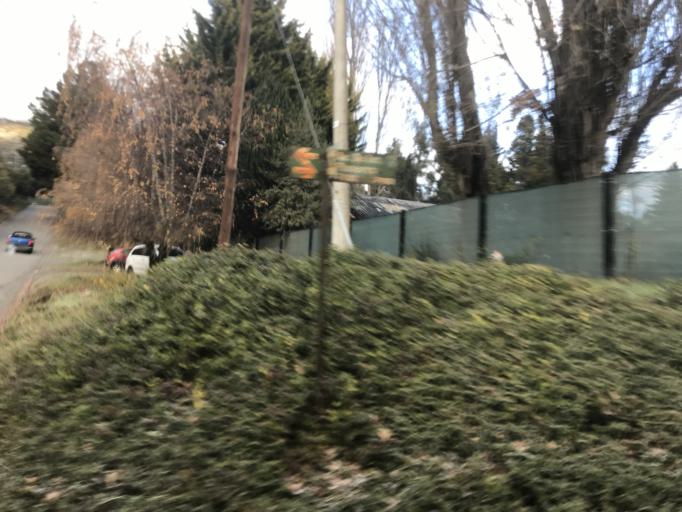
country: AR
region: Rio Negro
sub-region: Departamento de Bariloche
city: San Carlos de Bariloche
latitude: -41.1252
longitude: -71.3892
